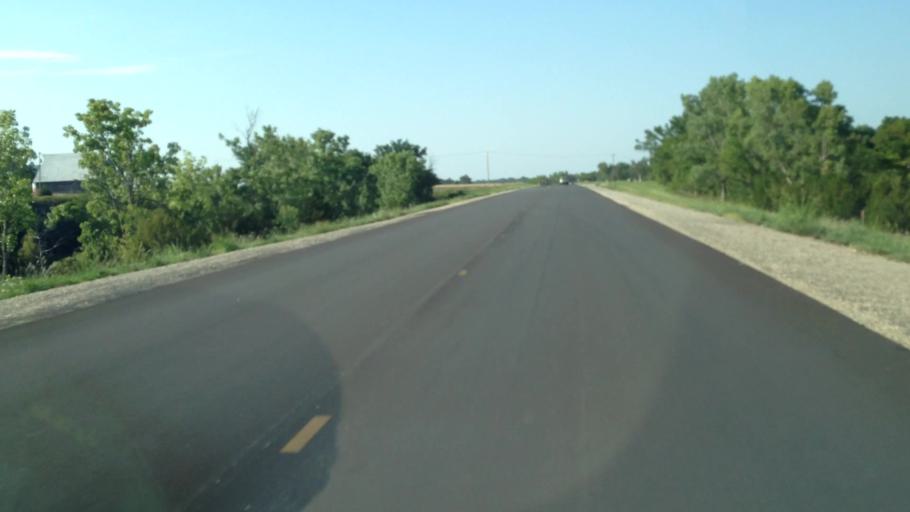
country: US
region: Kansas
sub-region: Anderson County
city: Garnett
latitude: 38.3228
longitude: -95.2507
